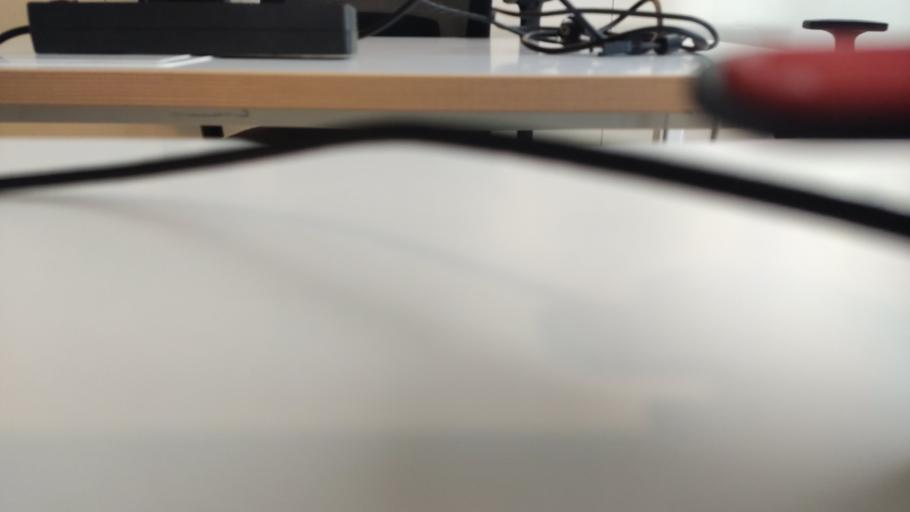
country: RU
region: Moskovskaya
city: Rogachevo
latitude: 56.4180
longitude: 37.0932
